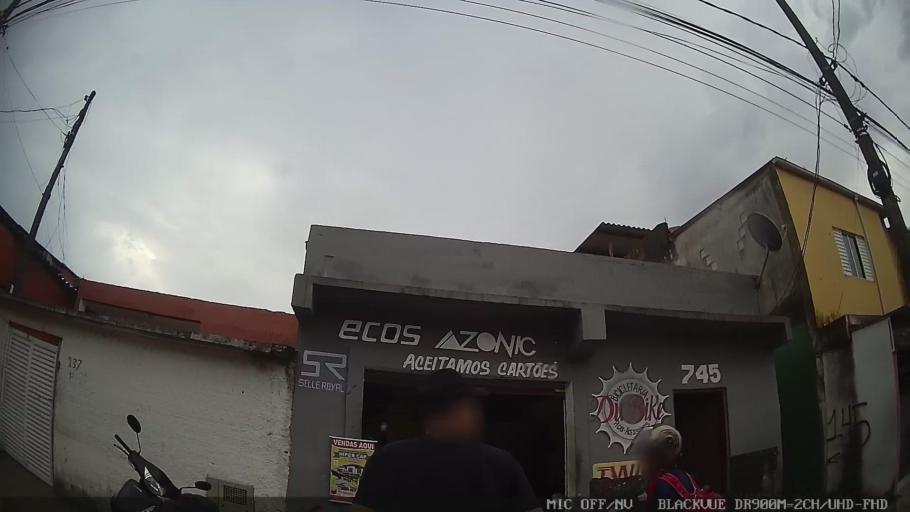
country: BR
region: Sao Paulo
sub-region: Guaruja
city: Guaruja
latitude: -23.9769
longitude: -46.2278
